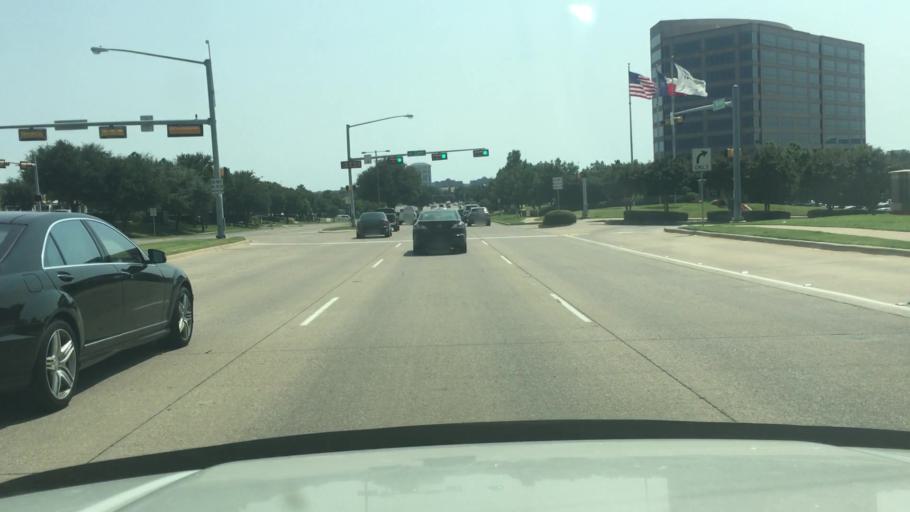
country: US
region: Texas
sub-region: Dallas County
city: Farmers Branch
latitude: 32.9006
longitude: -96.9589
